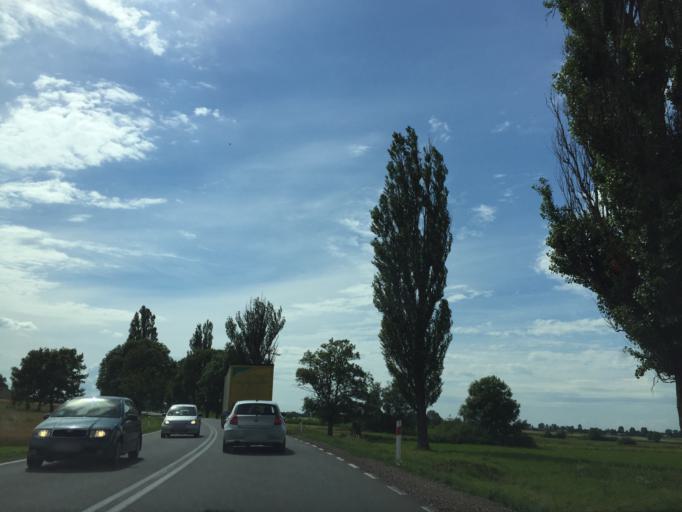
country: PL
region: Masovian Voivodeship
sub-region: Powiat losicki
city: Sarnaki
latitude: 52.2642
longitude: 22.8217
